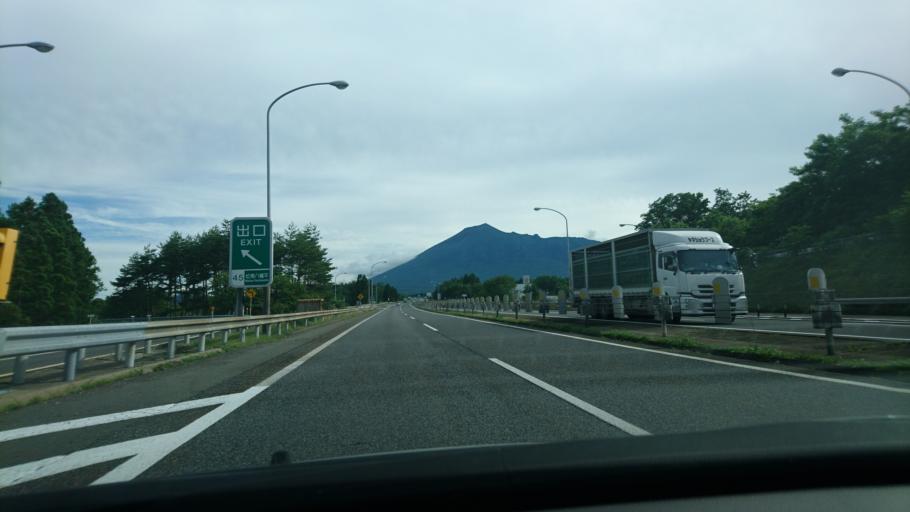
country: JP
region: Iwate
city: Shizukuishi
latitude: 39.9516
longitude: 141.0324
